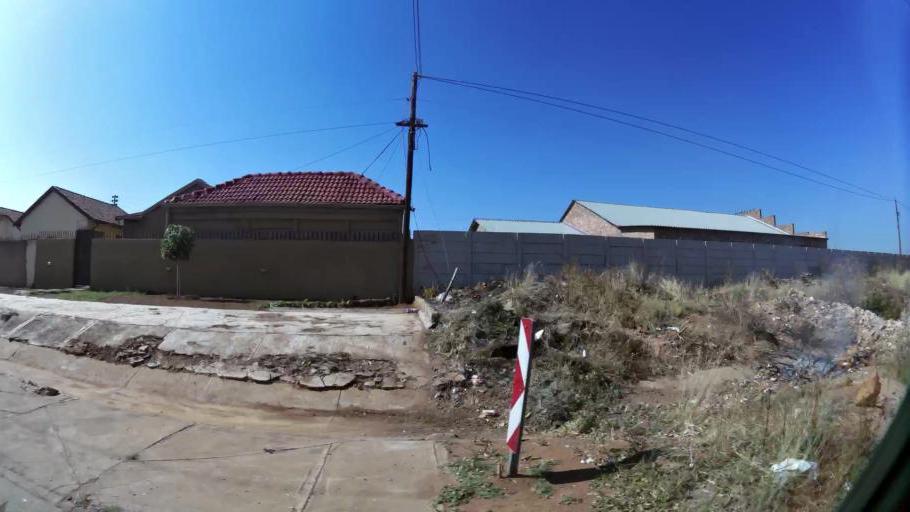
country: ZA
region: Gauteng
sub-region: City of Tshwane Metropolitan Municipality
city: Mabopane
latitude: -25.5558
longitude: 28.0740
